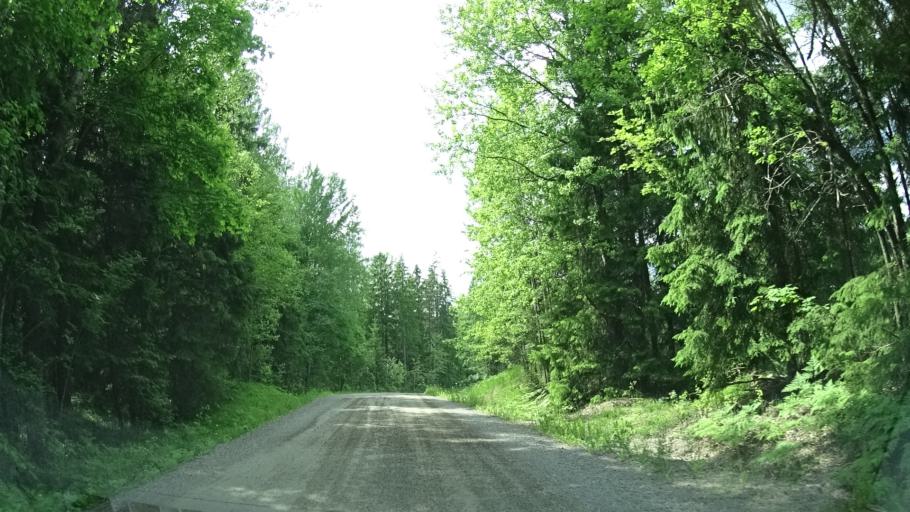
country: FI
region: Uusimaa
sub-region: Helsinki
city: Siuntio
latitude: 60.2126
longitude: 24.2816
